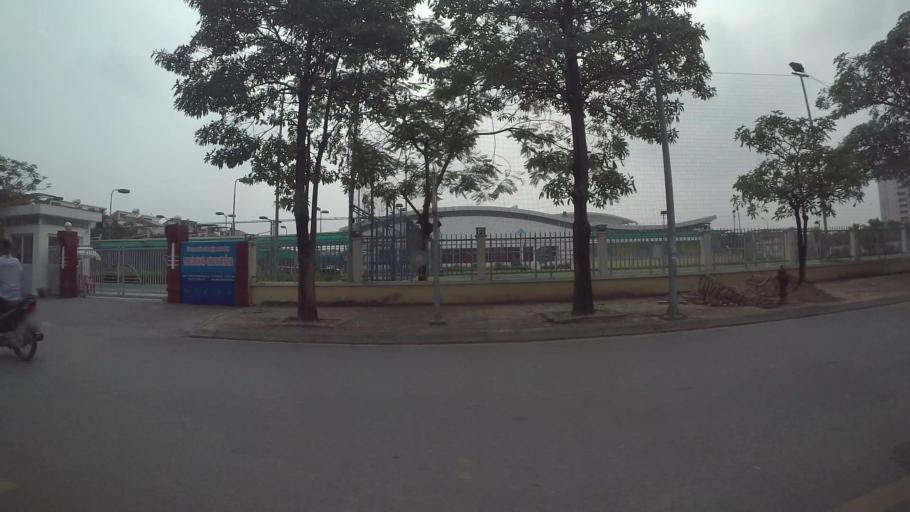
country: VN
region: Ha Noi
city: Trau Quy
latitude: 21.0563
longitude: 105.9086
